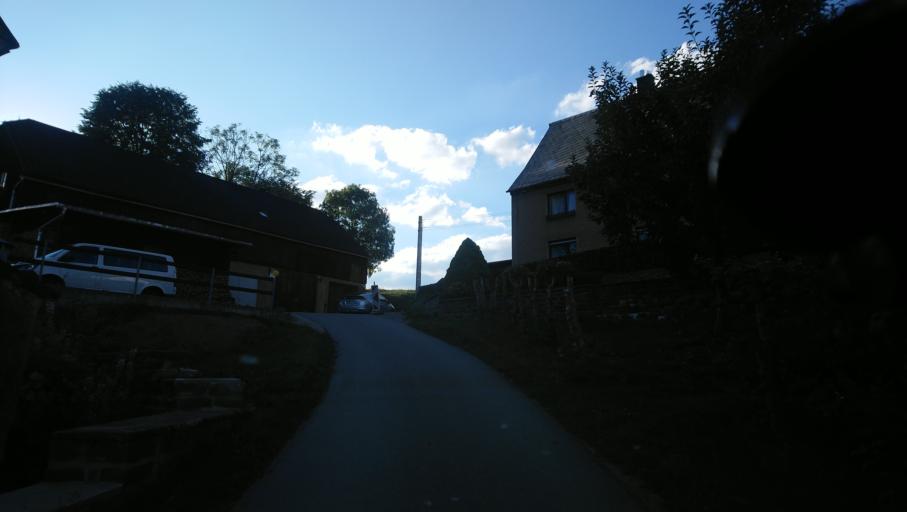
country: DE
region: Saxony
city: Schlettau
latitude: 50.5432
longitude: 12.9574
